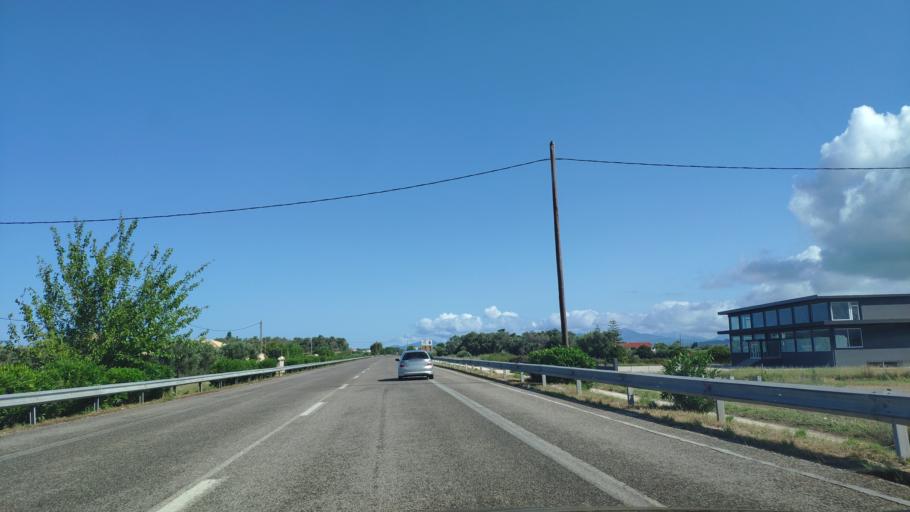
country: GR
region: Epirus
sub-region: Nomos Prevezis
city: Preveza
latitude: 38.9518
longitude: 20.7337
